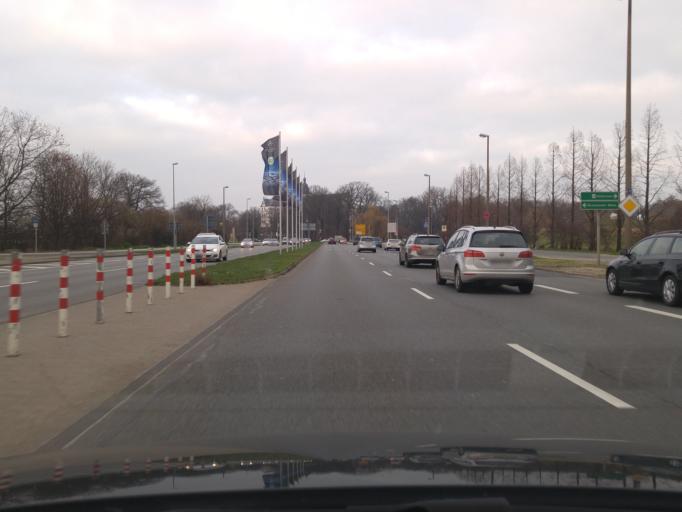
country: DE
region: Lower Saxony
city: Wolfsburg
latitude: 52.4346
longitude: 10.7994
